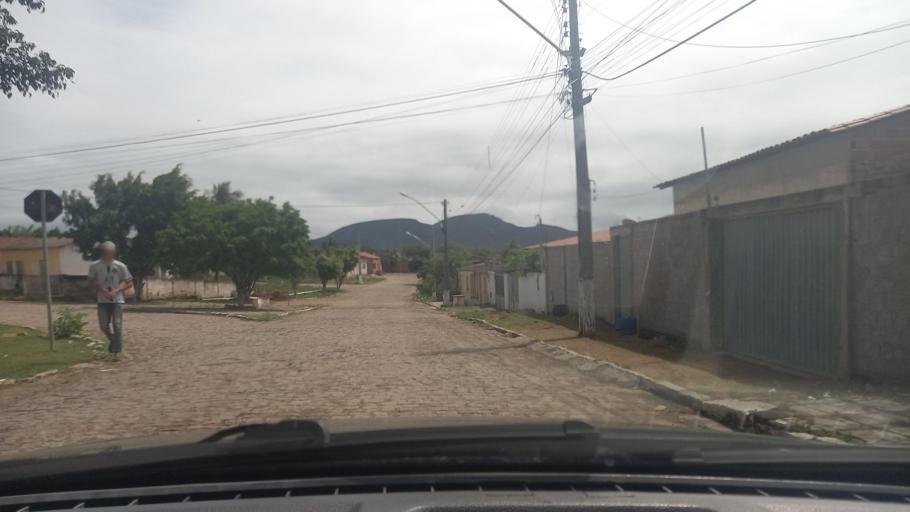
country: BR
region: Bahia
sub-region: Paulo Afonso
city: Paulo Afonso
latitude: -9.3435
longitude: -38.2596
